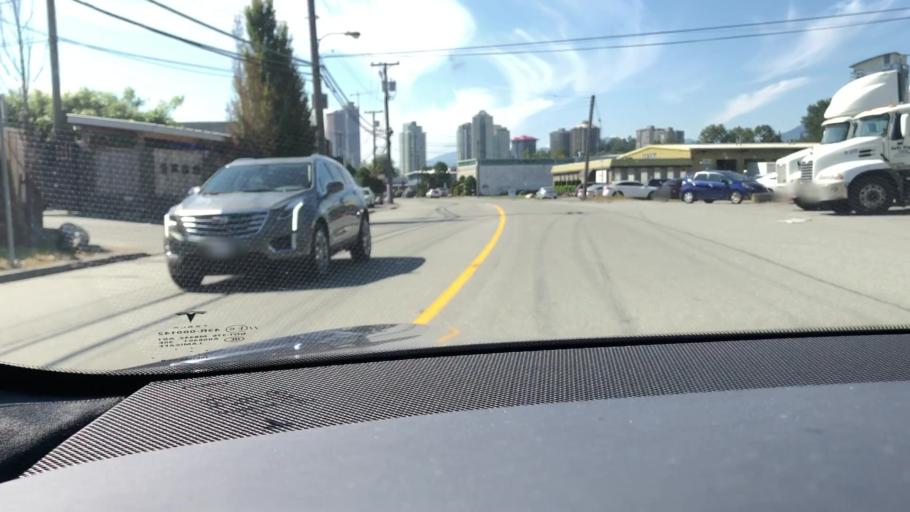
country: CA
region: British Columbia
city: Burnaby
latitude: 49.2582
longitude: -122.9786
